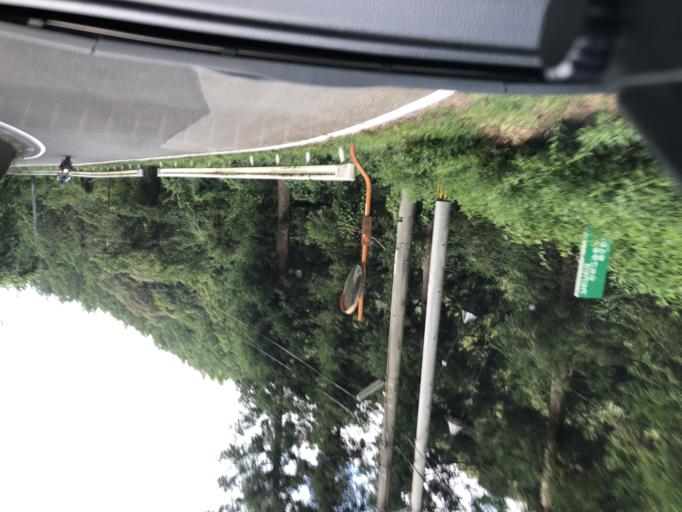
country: JP
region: Kochi
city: Kochi-shi
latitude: 33.6207
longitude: 133.4967
